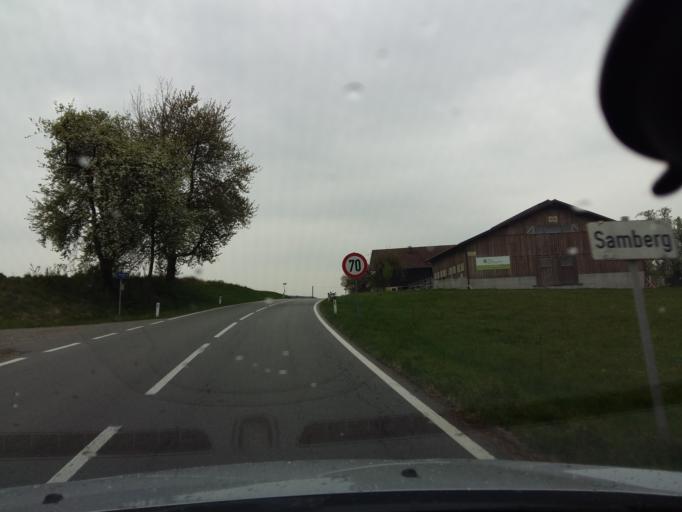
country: AT
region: Upper Austria
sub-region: Politischer Bezirk Scharding
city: Sankt Marienkirchen bei Schaerding
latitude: 48.4079
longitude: 13.4985
